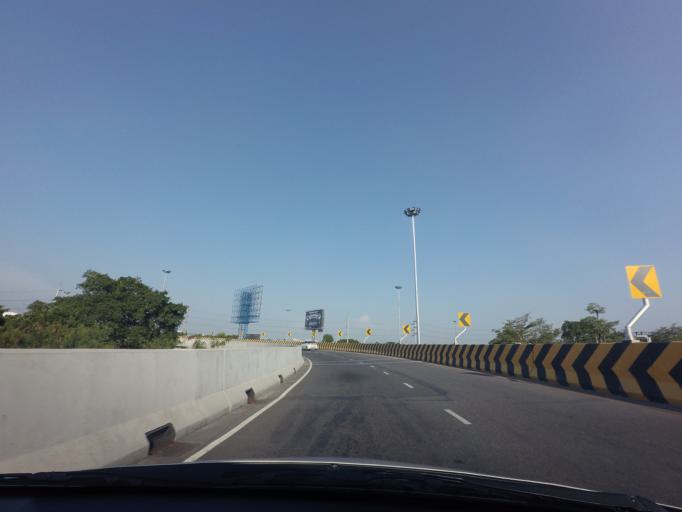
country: TH
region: Bangkok
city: Taling Chan
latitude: 13.7976
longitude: 100.4090
